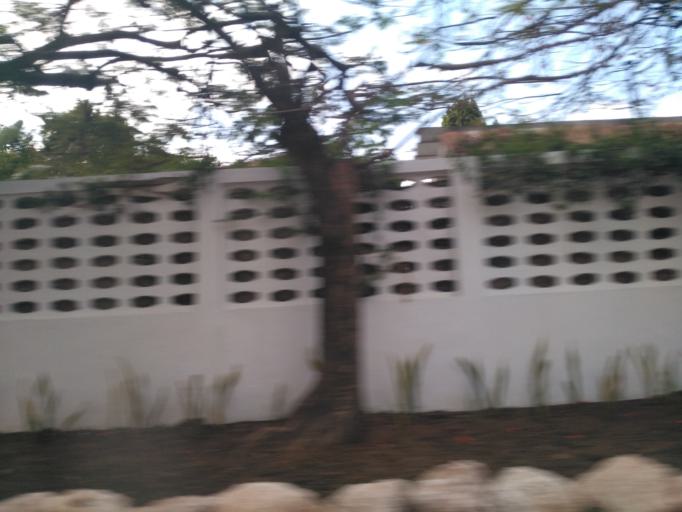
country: TZ
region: Dar es Salaam
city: Magomeni
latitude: -6.7606
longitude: 39.2675
